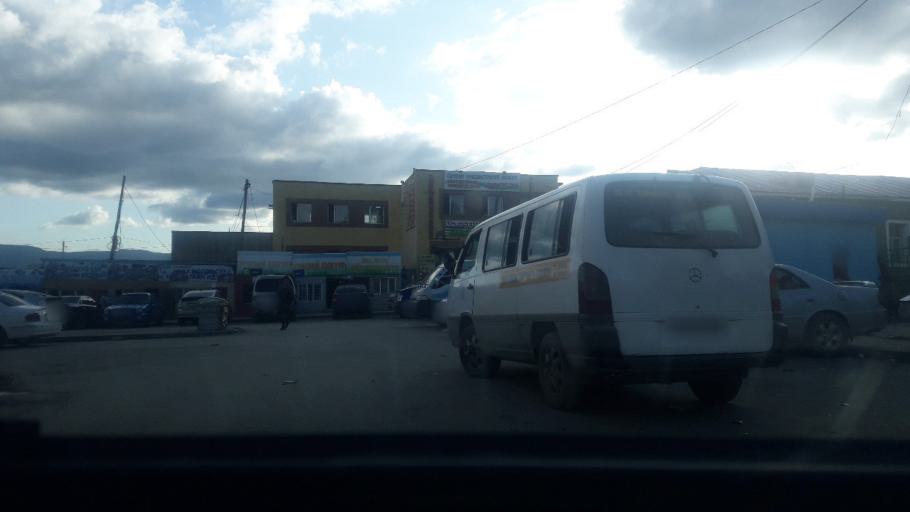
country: MN
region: Ulaanbaatar
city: Ulaanbaatar
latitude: 47.9348
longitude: 107.0056
